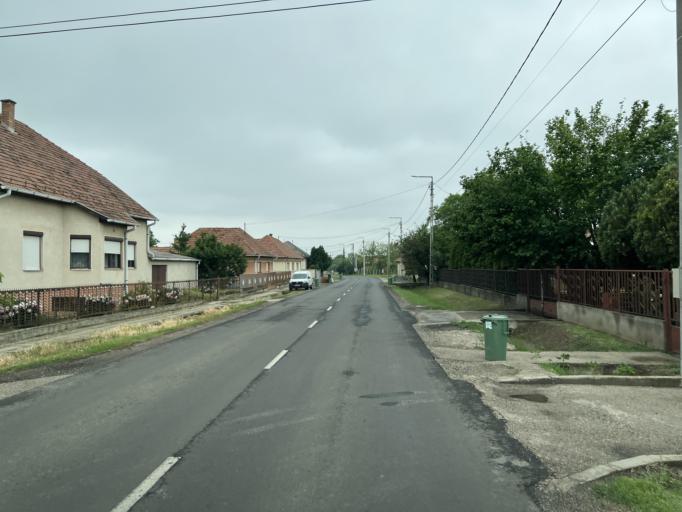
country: HU
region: Pest
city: Zsambok
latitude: 47.5503
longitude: 19.6051
